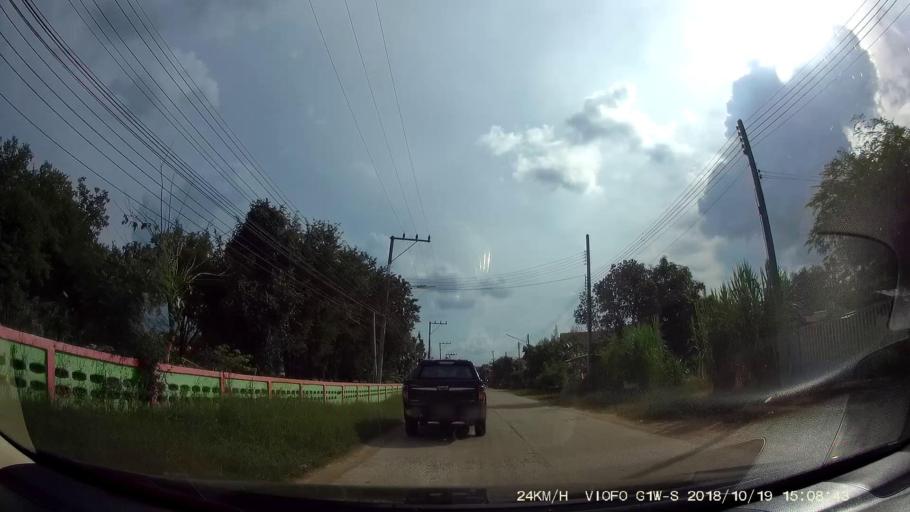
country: TH
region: Chaiyaphum
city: Phu Khiao
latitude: 16.4128
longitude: 102.1036
